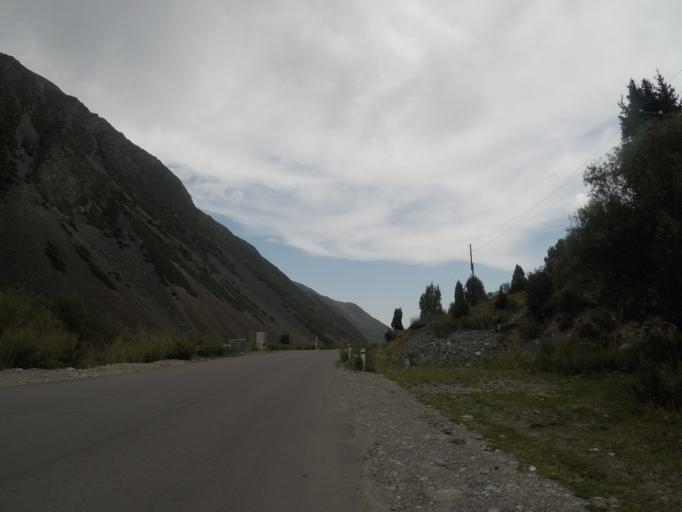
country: KG
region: Chuy
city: Bishkek
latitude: 42.5782
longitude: 74.4816
